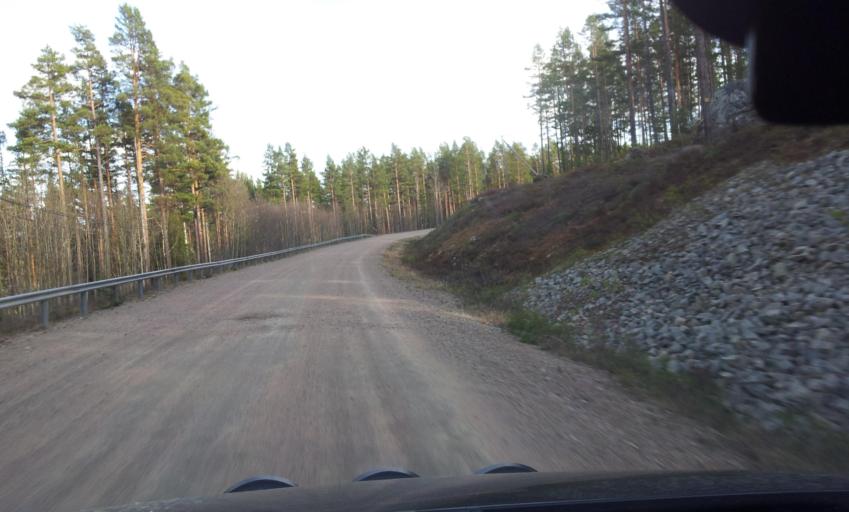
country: SE
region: Vaesternorrland
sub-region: Ange Kommun
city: Ange
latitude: 62.1666
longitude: 15.6556
